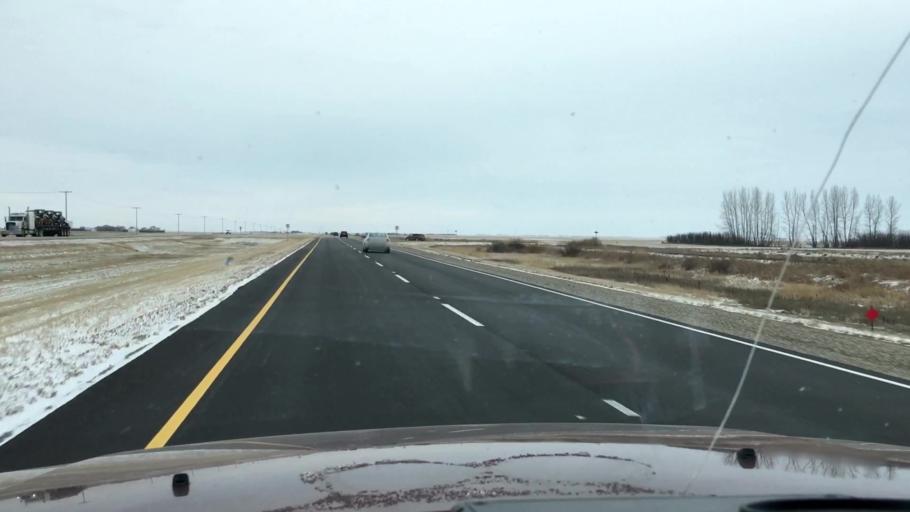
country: CA
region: Saskatchewan
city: Watrous
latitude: 51.1410
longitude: -105.9035
